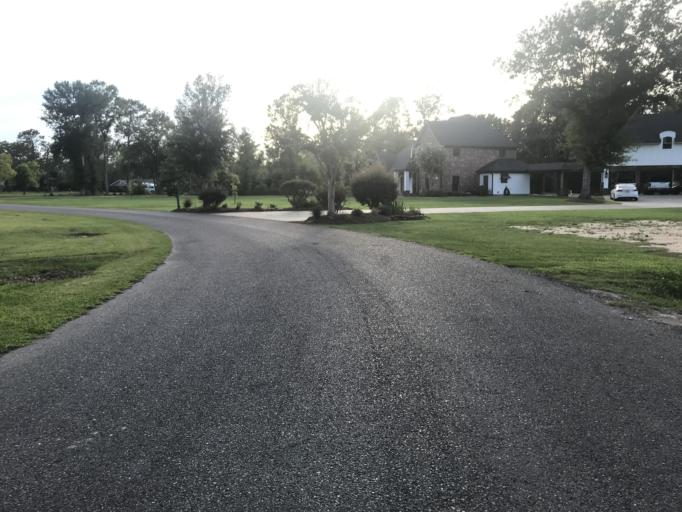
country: US
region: Louisiana
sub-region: Calcasieu Parish
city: Moss Bluff
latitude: 30.3400
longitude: -93.2593
